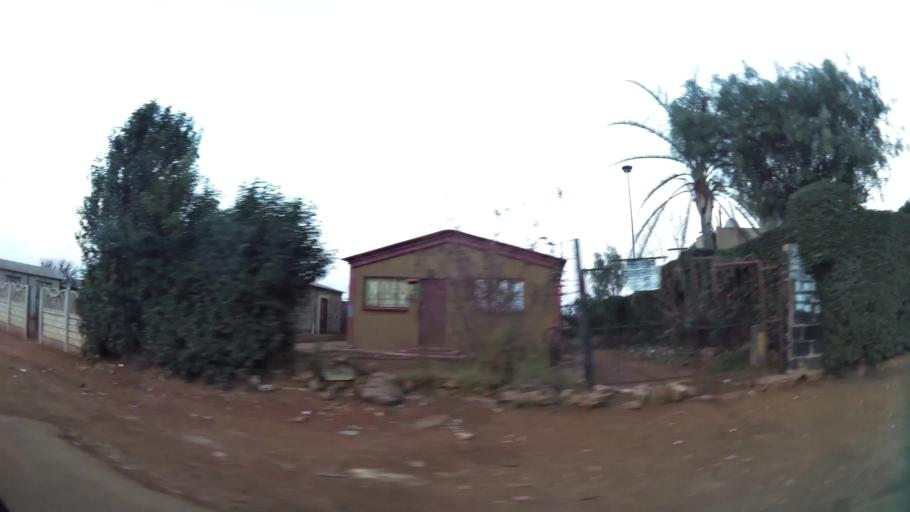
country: ZA
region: Gauteng
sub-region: City of Johannesburg Metropolitan Municipality
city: Orange Farm
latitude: -26.5560
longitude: 27.8611
